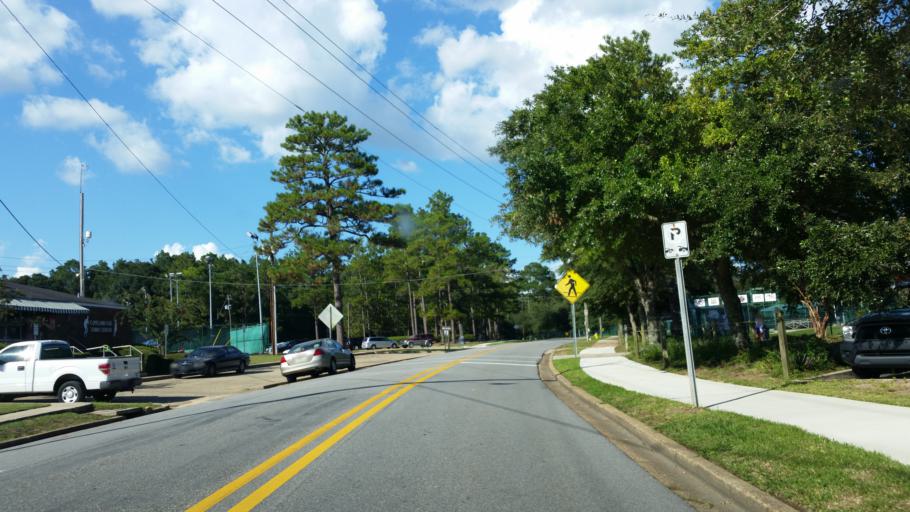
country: US
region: Alabama
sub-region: Mobile County
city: Prichard
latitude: 30.7075
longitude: -88.1644
